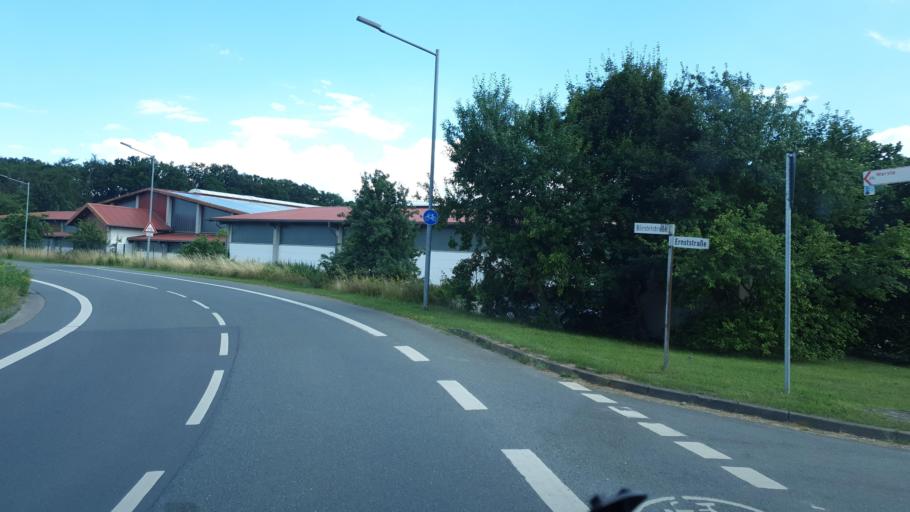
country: DE
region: North Rhine-Westphalia
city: Loehne
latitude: 52.2103
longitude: 8.7429
